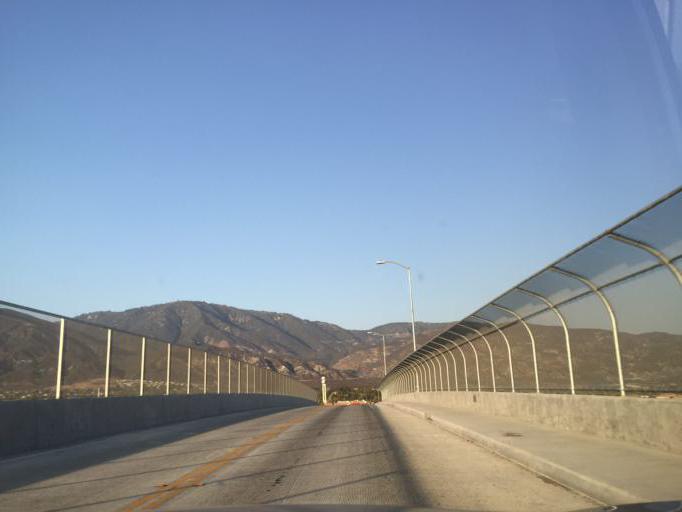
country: US
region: California
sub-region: San Bernardino County
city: Muscoy
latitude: 34.1876
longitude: -117.3648
